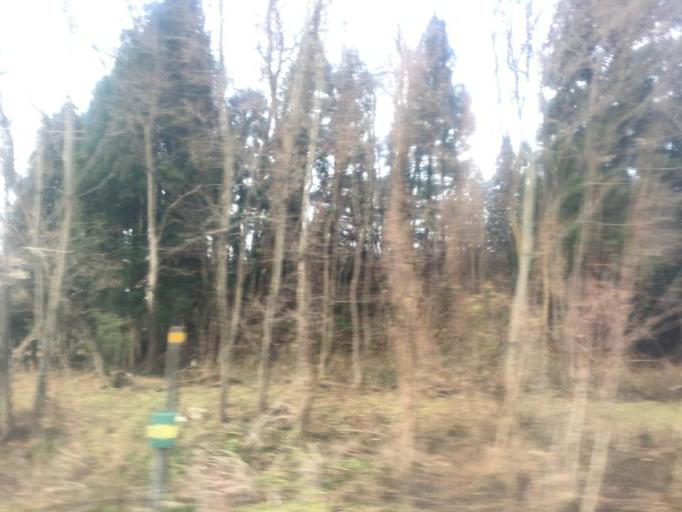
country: JP
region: Akita
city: Odate
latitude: 40.2981
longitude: 140.5666
